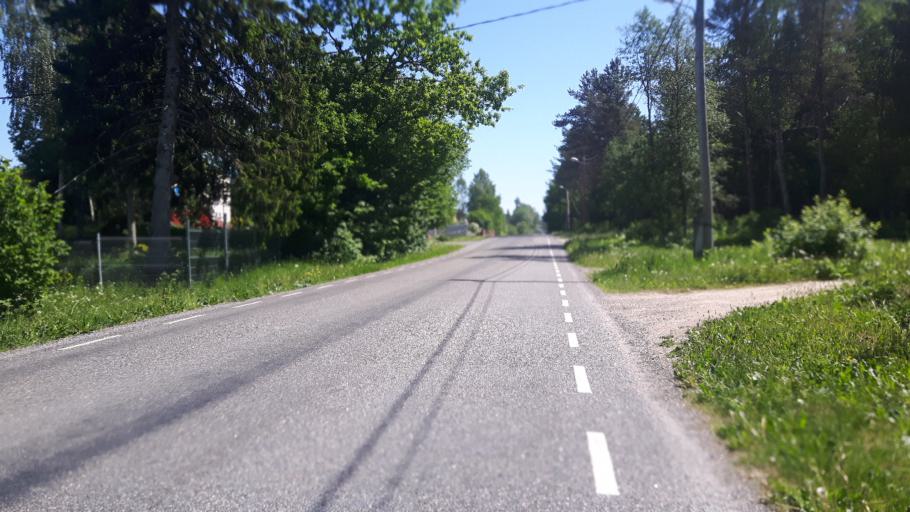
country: EE
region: Raplamaa
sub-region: Kohila vald
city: Kohila
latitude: 59.1741
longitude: 24.7334
